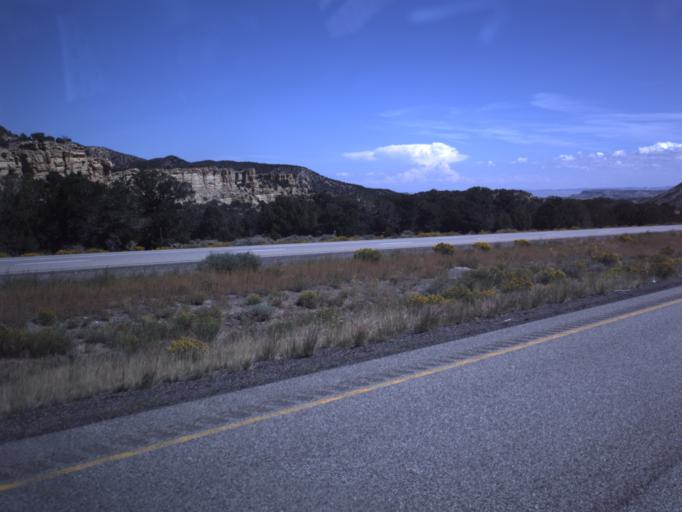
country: US
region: Utah
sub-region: Emery County
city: Ferron
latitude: 38.7553
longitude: -111.3941
